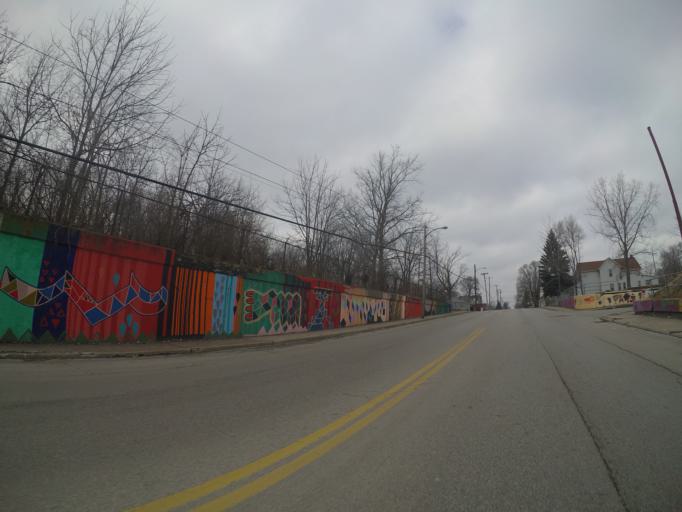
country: US
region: Ohio
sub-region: Lucas County
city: Oregon
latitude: 41.6256
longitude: -83.5153
